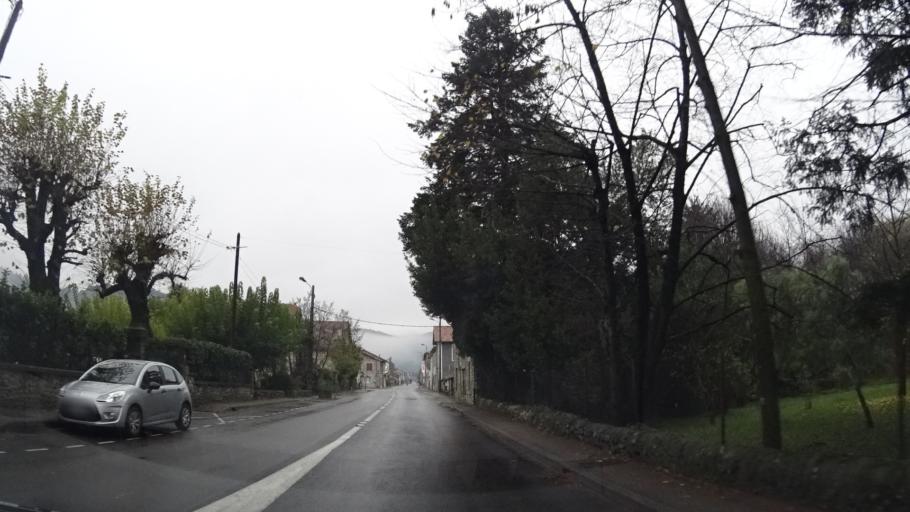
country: FR
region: Rhone-Alpes
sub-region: Departement de l'Ardeche
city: Labegude
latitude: 44.6487
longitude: 4.3239
